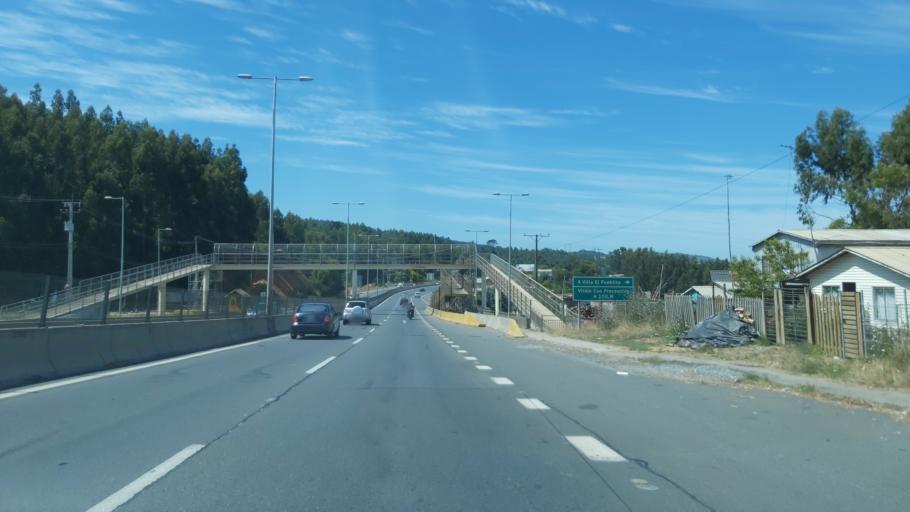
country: CL
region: Biobio
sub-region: Provincia de Concepcion
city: Coronel
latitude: -37.0551
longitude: -73.1402
